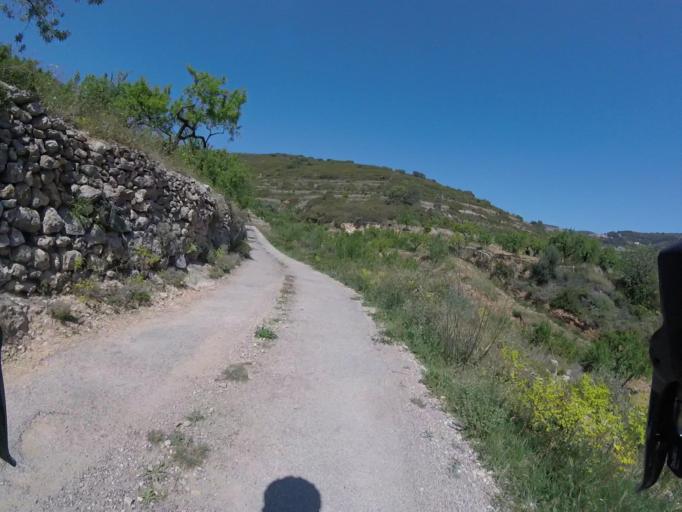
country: ES
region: Valencia
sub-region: Provincia de Castello
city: Sierra-Engarceran
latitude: 40.2544
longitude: -0.0255
